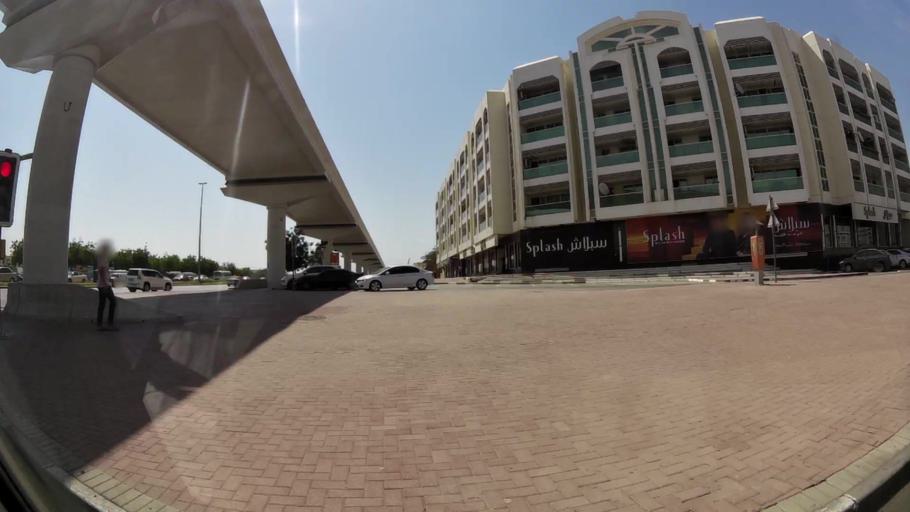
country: AE
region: Ash Shariqah
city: Sharjah
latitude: 25.2750
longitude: 55.3667
